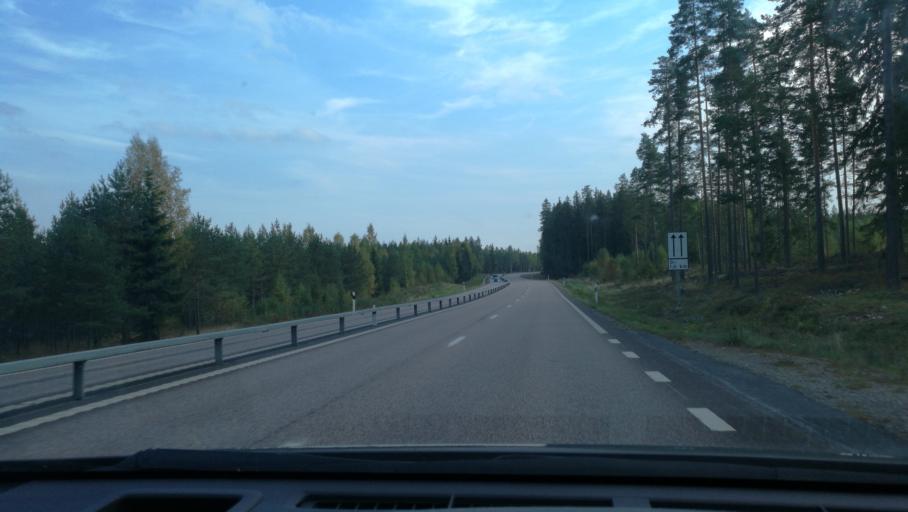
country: SE
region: Dalarna
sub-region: Avesta Kommun
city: Avesta
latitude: 60.0499
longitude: 16.3398
